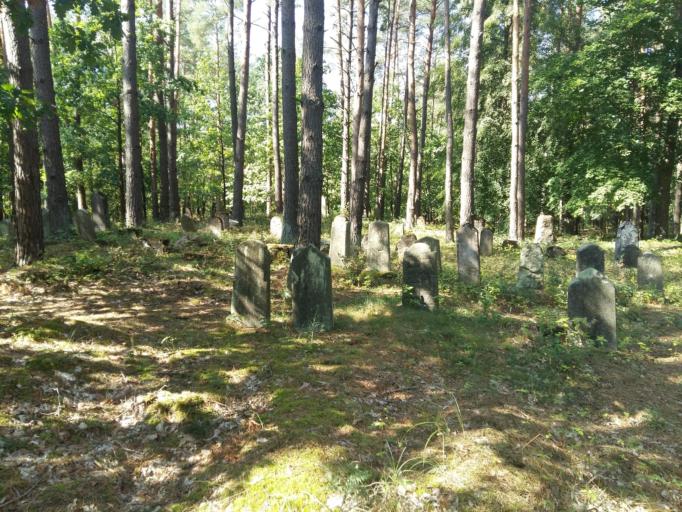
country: LT
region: Alytaus apskritis
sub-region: Alytaus rajonas
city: Daugai
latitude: 54.1601
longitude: 24.1922
